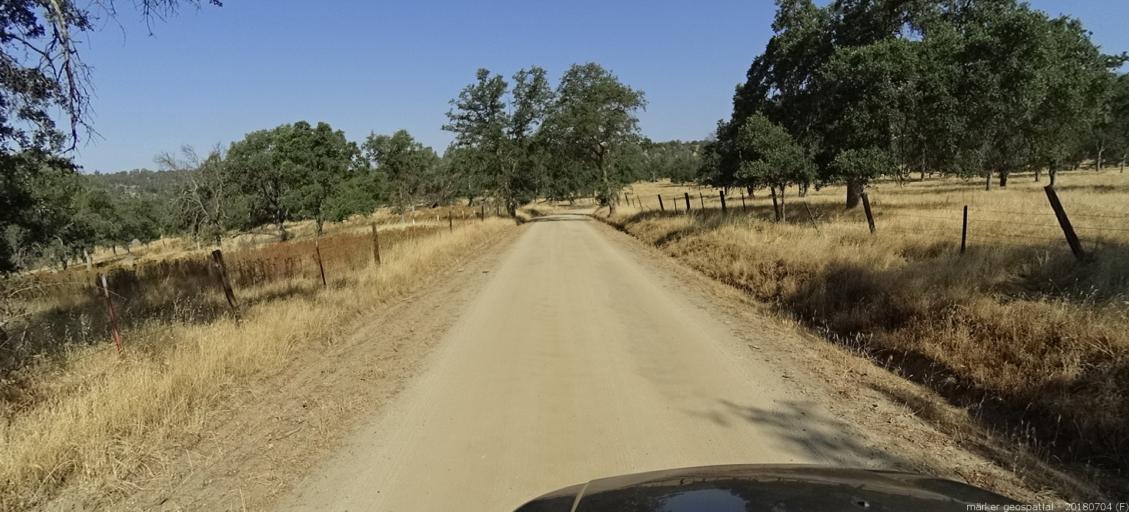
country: US
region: California
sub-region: Fresno County
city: Auberry
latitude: 37.1024
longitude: -119.6312
